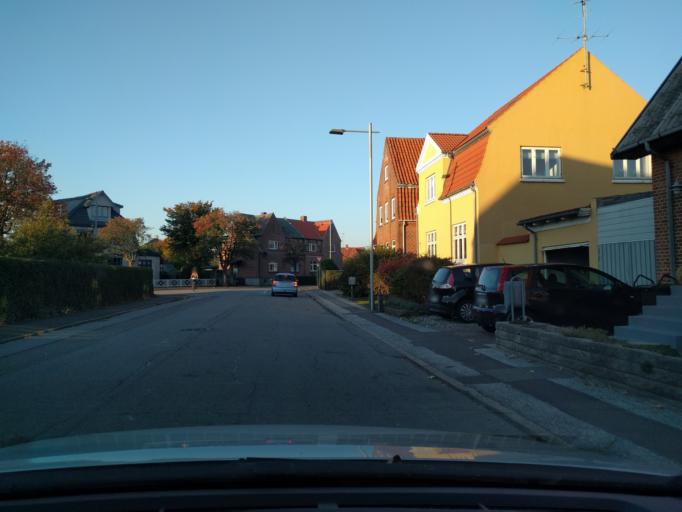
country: DK
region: Zealand
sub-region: Guldborgsund Kommune
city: Nykobing Falster
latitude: 54.7648
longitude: 11.8861
